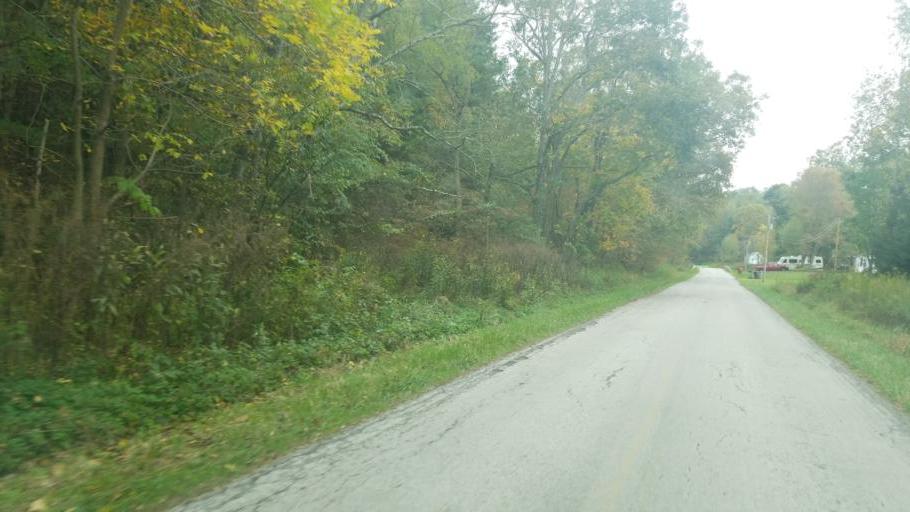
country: US
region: Ohio
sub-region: Ashland County
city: Loudonville
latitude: 40.5826
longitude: -82.1679
